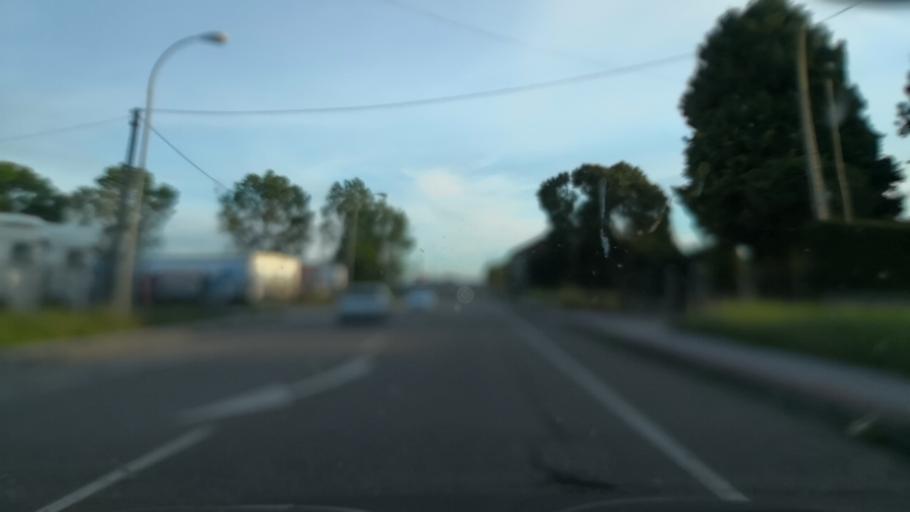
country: ES
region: Galicia
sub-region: Provincia de Ourense
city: Verin
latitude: 41.9295
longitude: -7.4411
